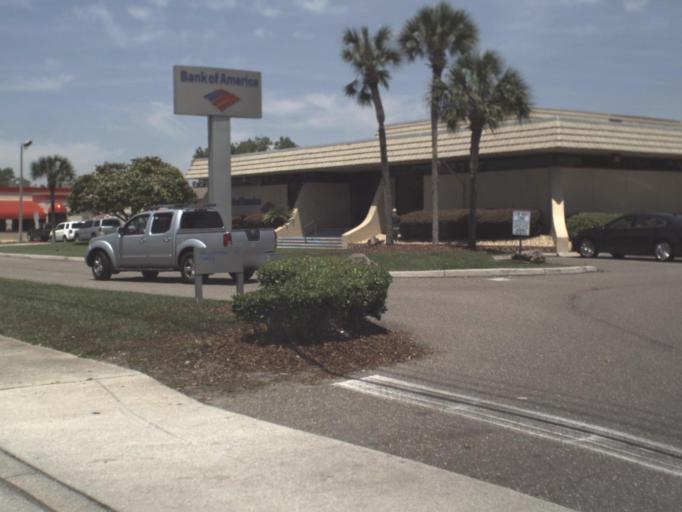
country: US
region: Florida
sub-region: Saint Johns County
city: Fruit Cove
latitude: 30.2210
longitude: -81.5668
